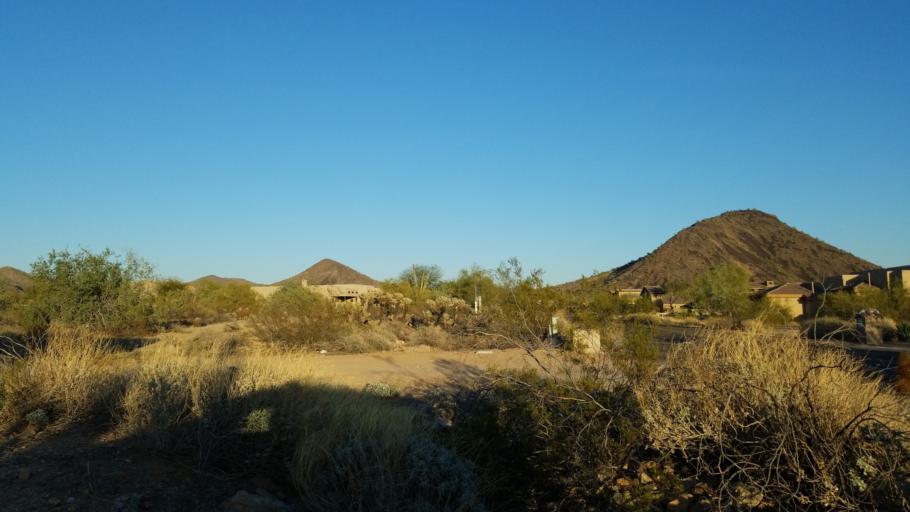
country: US
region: Arizona
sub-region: Maricopa County
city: Fountain Hills
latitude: 33.5807
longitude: -111.7985
